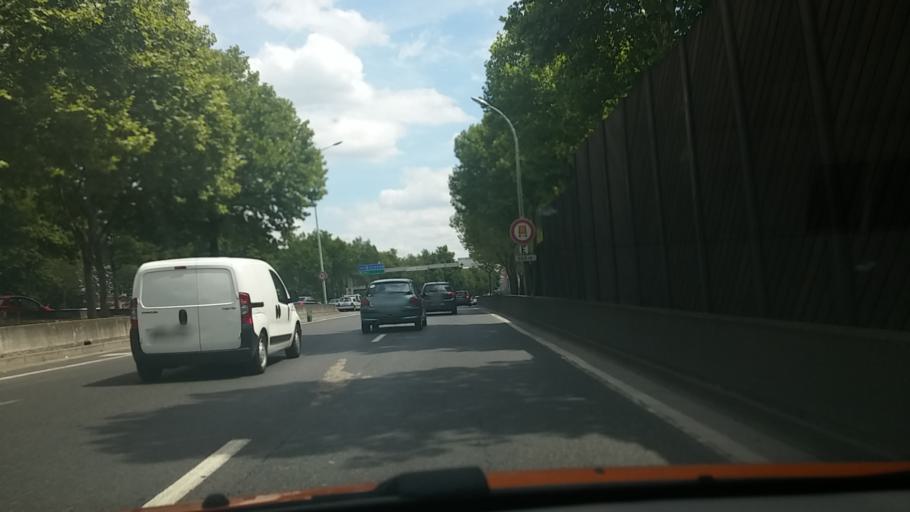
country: FR
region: Ile-de-France
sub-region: Departement de Seine-Saint-Denis
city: Aubervilliers
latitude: 48.9005
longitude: 2.3632
